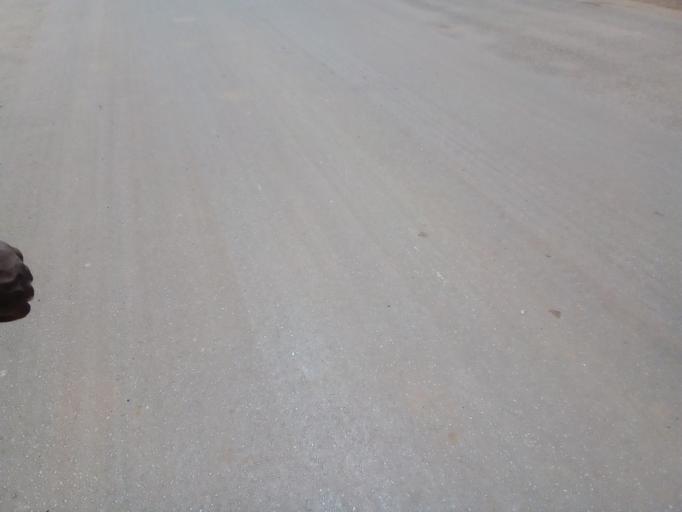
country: GH
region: Upper East
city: Navrongo
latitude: 11.0006
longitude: -1.1152
